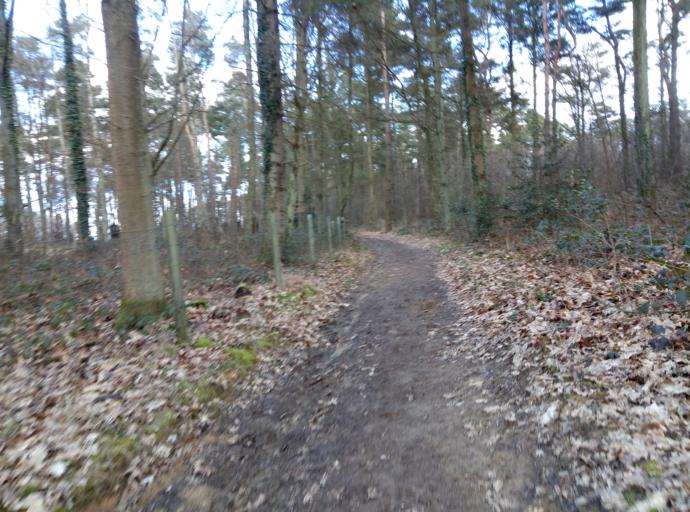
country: BE
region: Flanders
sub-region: Provincie Vlaams-Brabant
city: Oud-Heverlee
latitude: 50.8150
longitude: 4.6688
